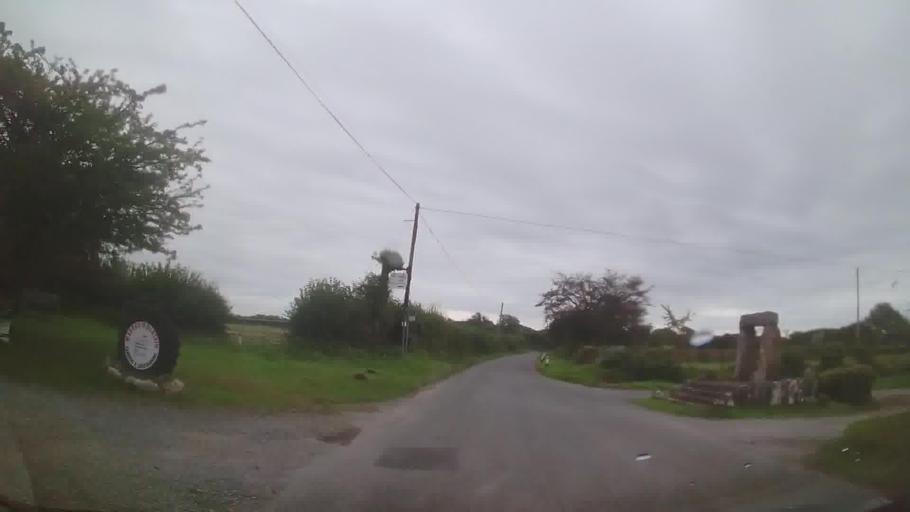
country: GB
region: Wales
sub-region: Carmarthenshire
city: Whitland
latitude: 51.7508
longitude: -4.5985
